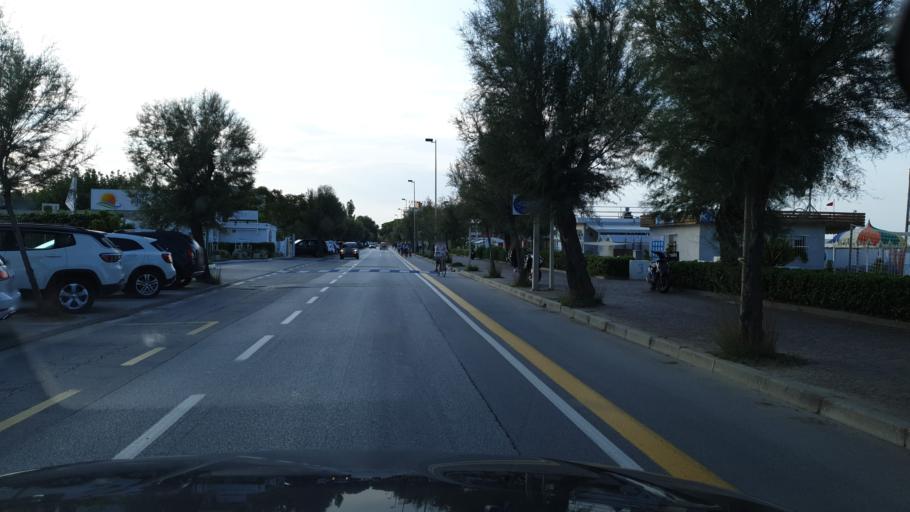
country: IT
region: Emilia-Romagna
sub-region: Provincia di Rimini
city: Misano Adriatico
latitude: 43.9861
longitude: 12.6881
